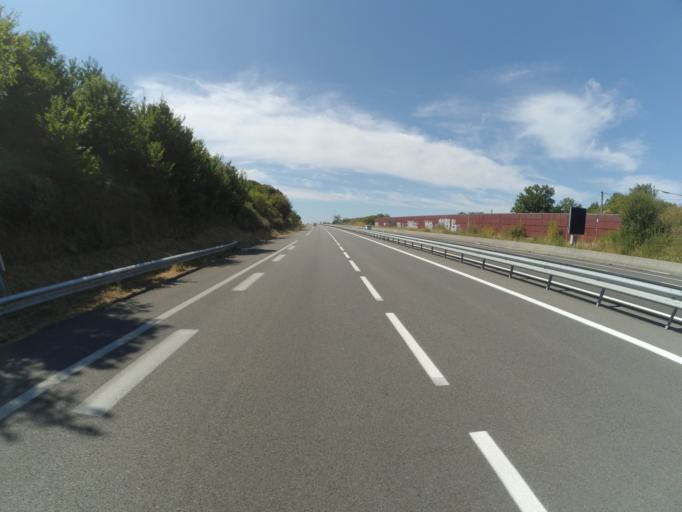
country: FR
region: Limousin
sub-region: Departement de la Haute-Vienne
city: Saint-Victurnien
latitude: 45.8966
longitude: 1.0309
